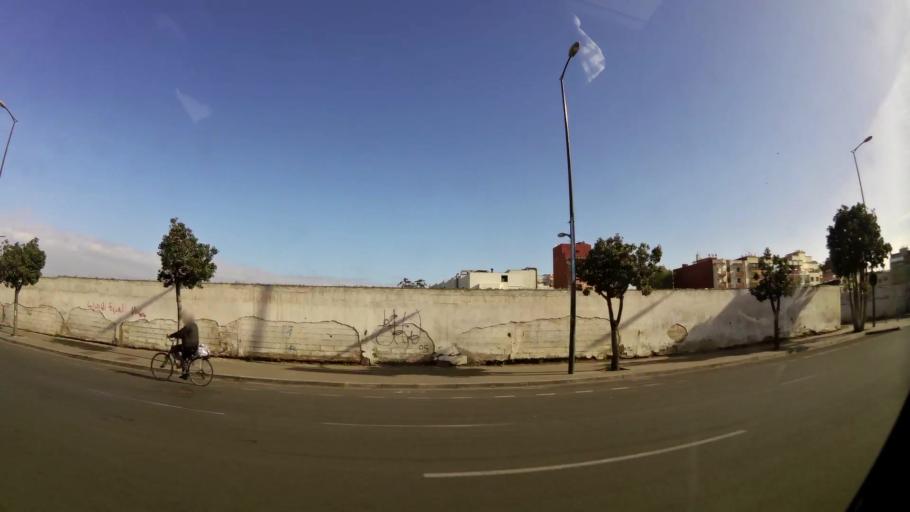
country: MA
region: Grand Casablanca
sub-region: Casablanca
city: Casablanca
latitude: 33.5976
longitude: -7.5901
